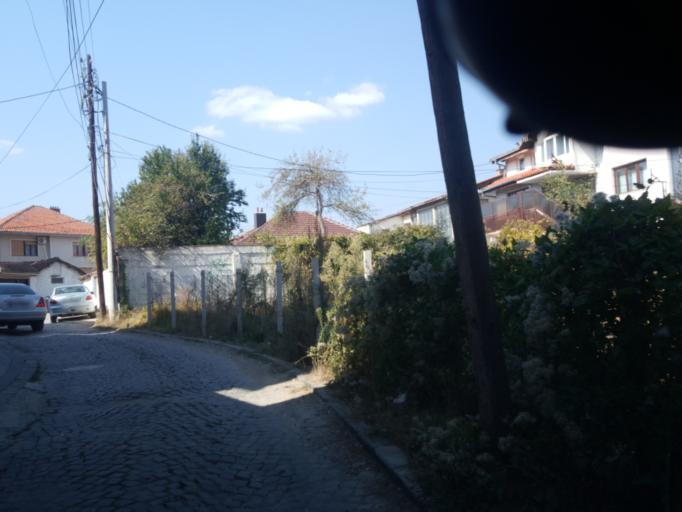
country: XK
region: Gjakova
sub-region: Komuna e Gjakoves
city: Gjakove
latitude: 42.3831
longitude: 20.4271
